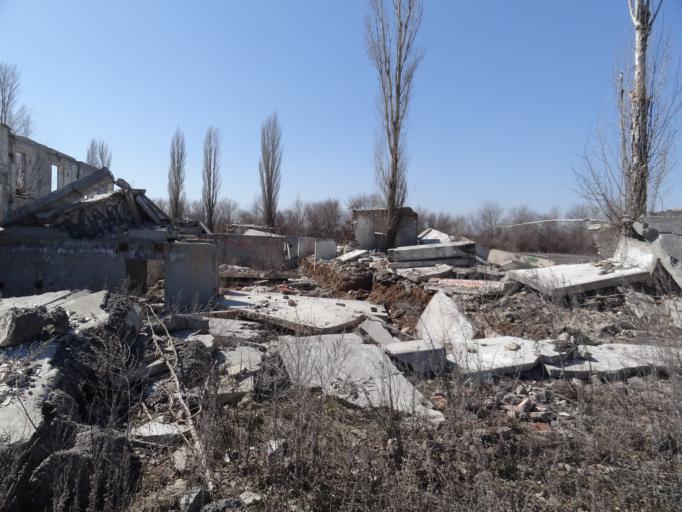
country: RU
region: Saratov
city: Shumeyka
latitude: 51.4081
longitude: 46.2445
